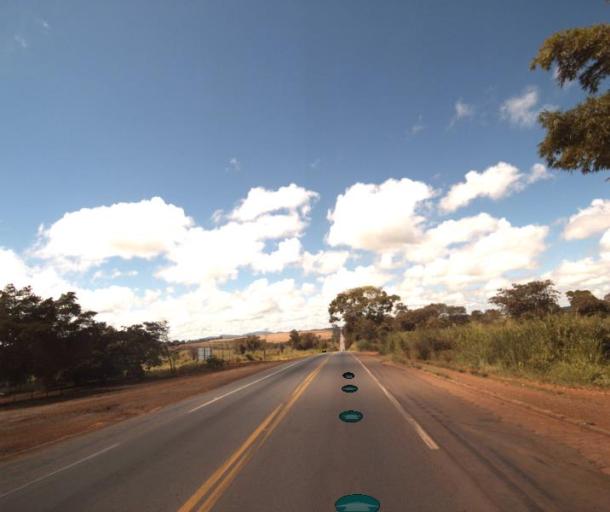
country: BR
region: Goias
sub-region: Jaragua
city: Jaragua
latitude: -15.8598
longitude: -49.2616
